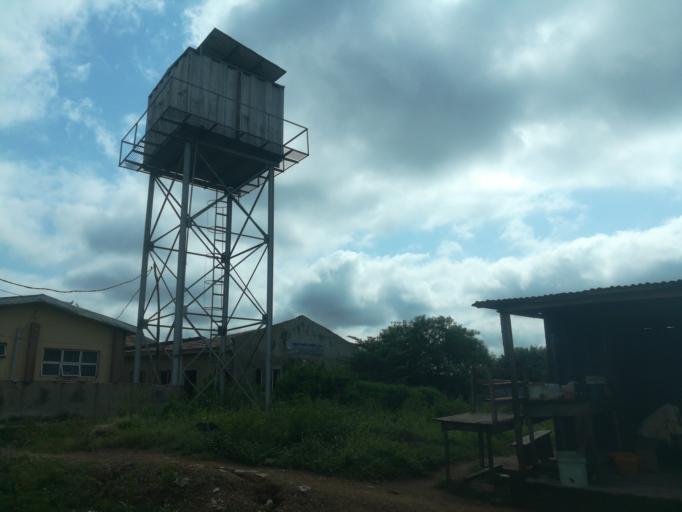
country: NG
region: Oyo
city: Ibadan
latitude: 7.3331
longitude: 3.8573
